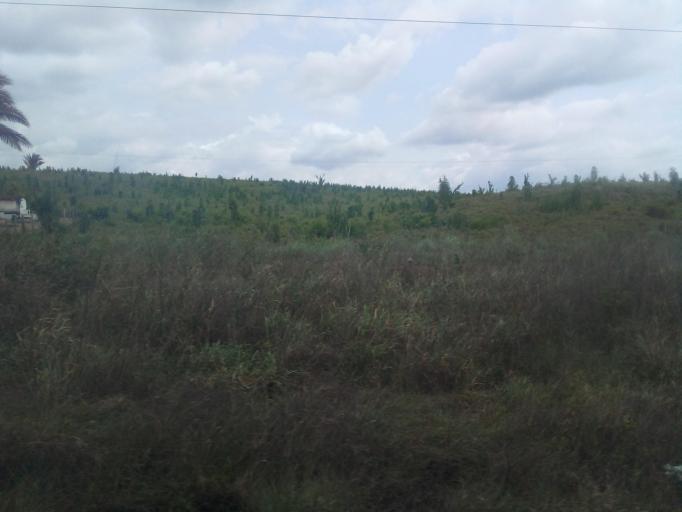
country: BR
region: Maranhao
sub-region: Santa Ines
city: Santa Ines
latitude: -3.7075
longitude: -46.0286
